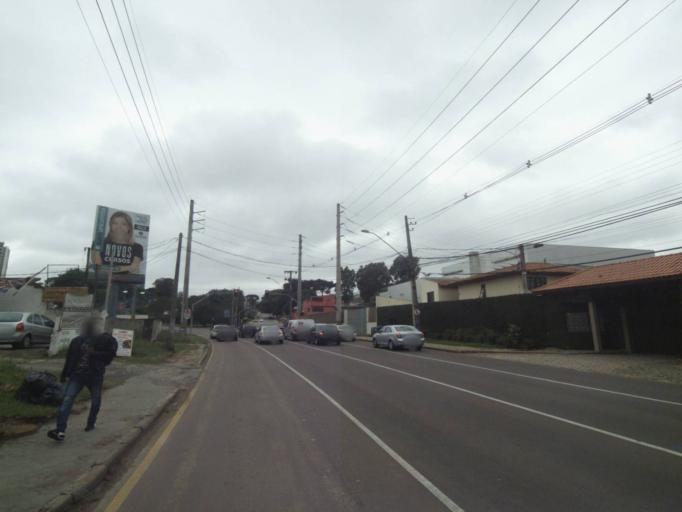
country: BR
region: Parana
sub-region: Curitiba
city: Curitiba
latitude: -25.4400
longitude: -49.3159
